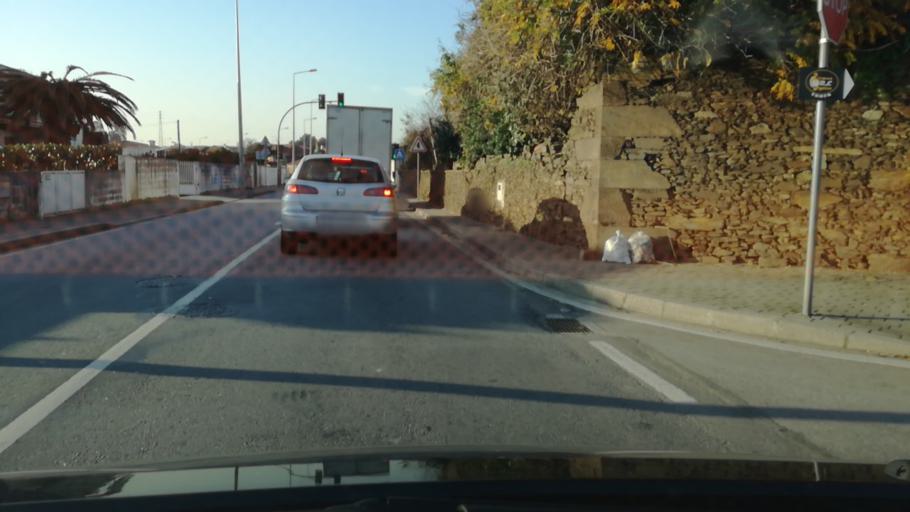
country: PT
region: Porto
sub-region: Trofa
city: Bougado
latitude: 41.3397
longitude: -8.5389
